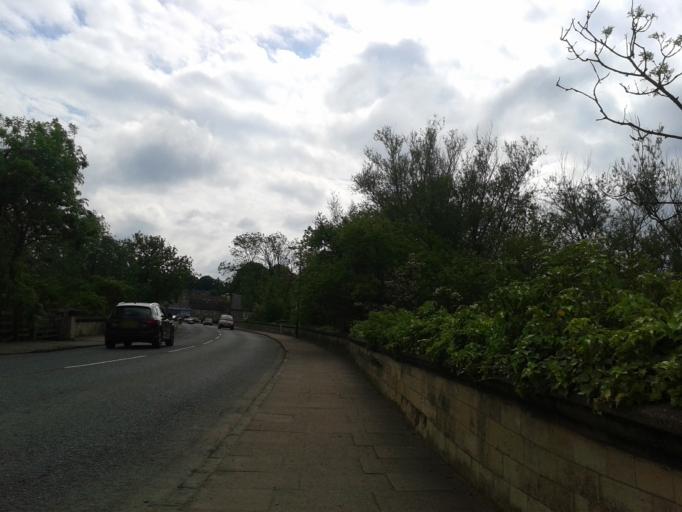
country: GB
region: England
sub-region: Northamptonshire
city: Oundle
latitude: 52.4879
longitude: -0.4631
